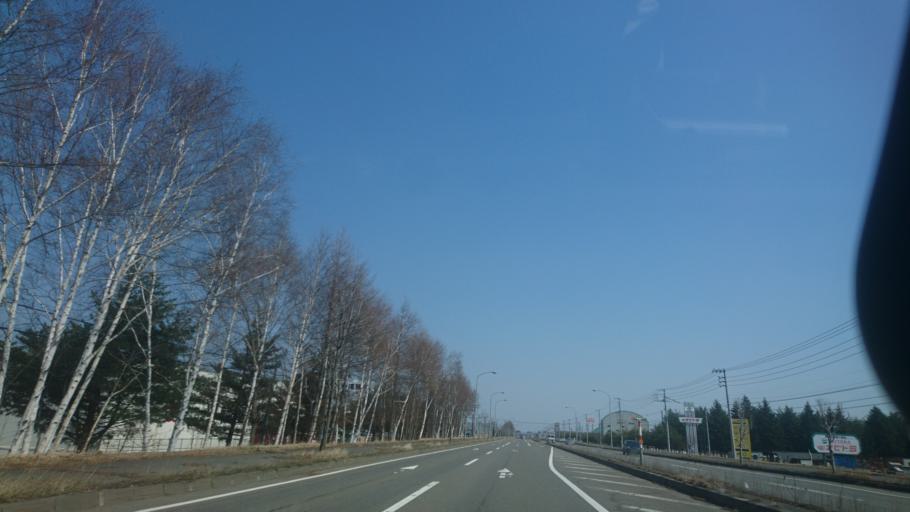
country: JP
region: Hokkaido
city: Obihiro
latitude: 42.9240
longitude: 143.0920
